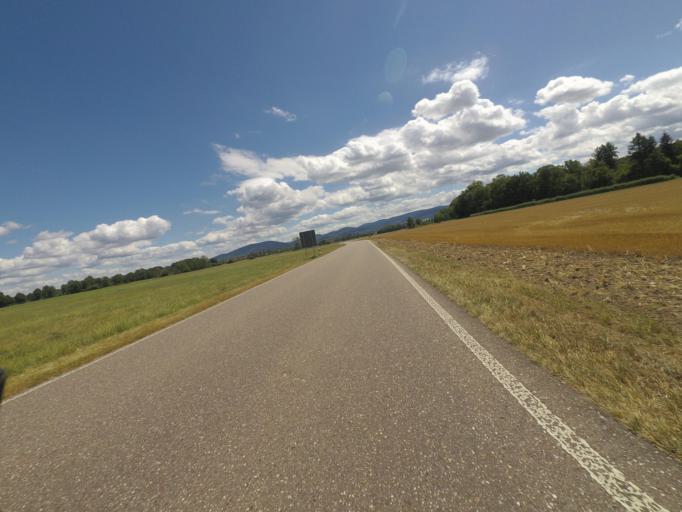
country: DE
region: Baden-Wuerttemberg
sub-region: Karlsruhe Region
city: Schwarzach
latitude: 48.7536
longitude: 8.0796
